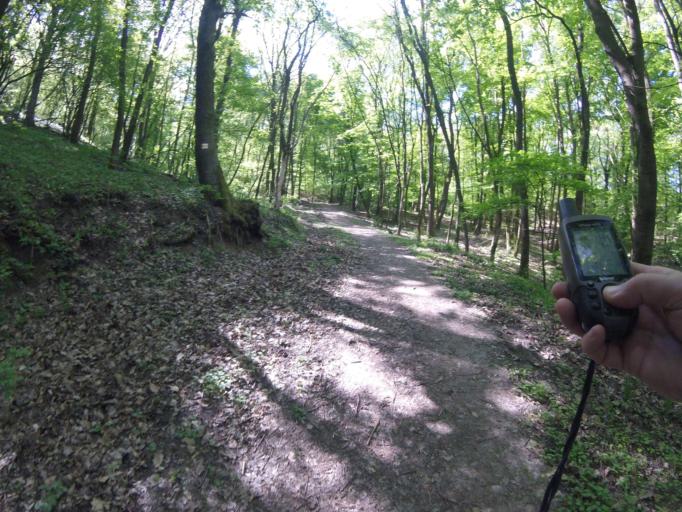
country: HU
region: Pest
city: Nagymaros
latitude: 47.7922
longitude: 18.9193
